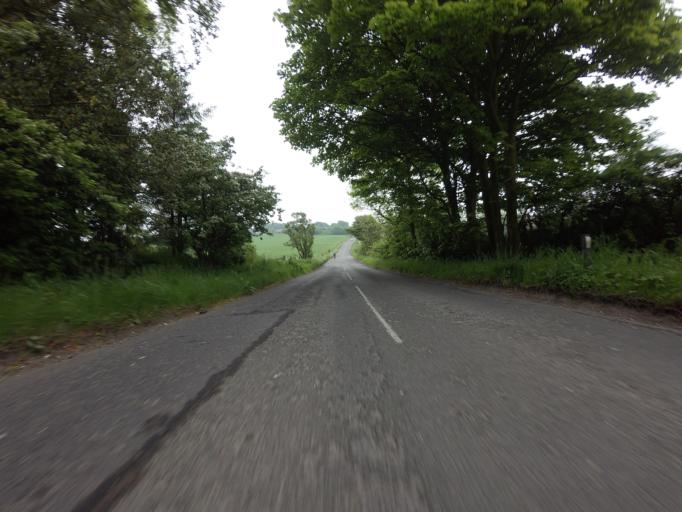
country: GB
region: Scotland
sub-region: Fife
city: Townhill
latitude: 56.1025
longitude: -3.4513
